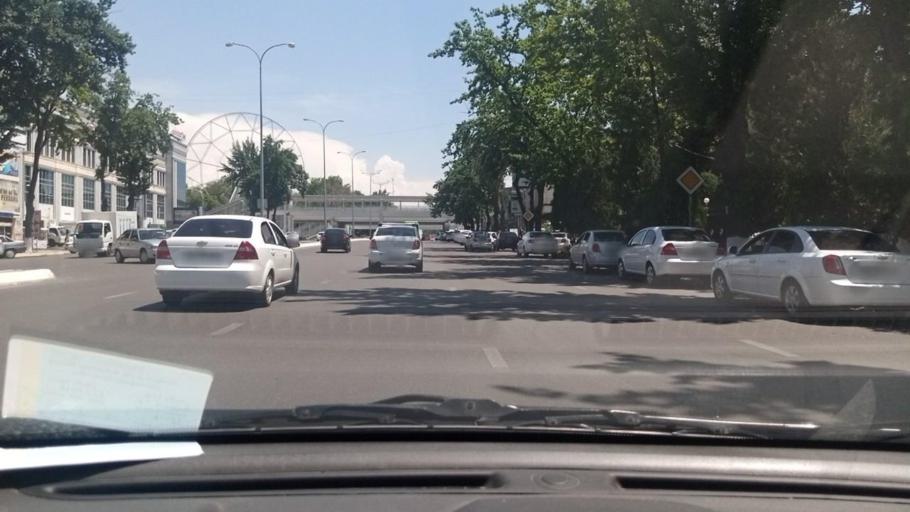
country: UZ
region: Toshkent Shahri
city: Tashkent
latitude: 41.2835
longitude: 69.2102
